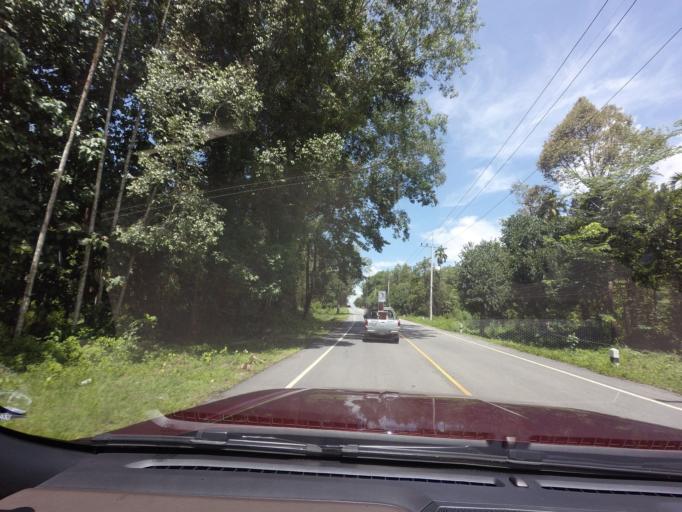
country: TH
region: Narathiwat
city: Chanae
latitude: 6.1485
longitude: 101.7039
